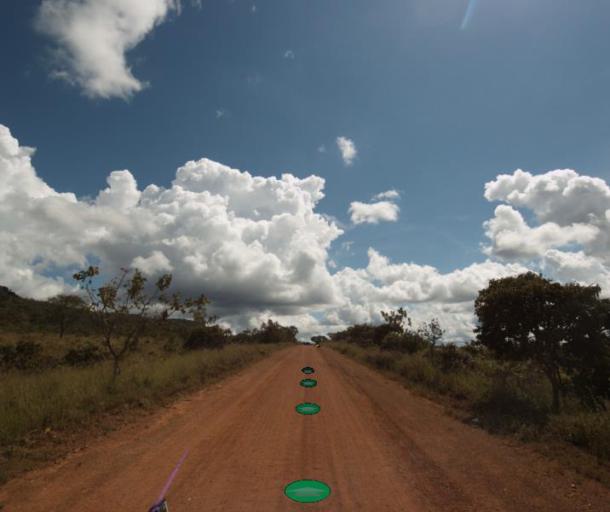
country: BR
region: Goias
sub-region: Pirenopolis
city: Pirenopolis
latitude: -15.7807
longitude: -48.8313
